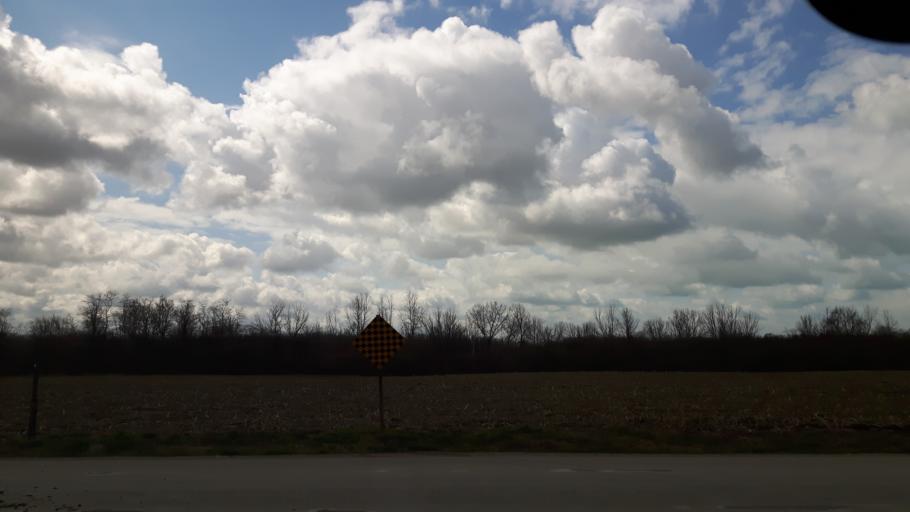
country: CA
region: Ontario
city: Bluewater
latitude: 43.5435
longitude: -81.7009
